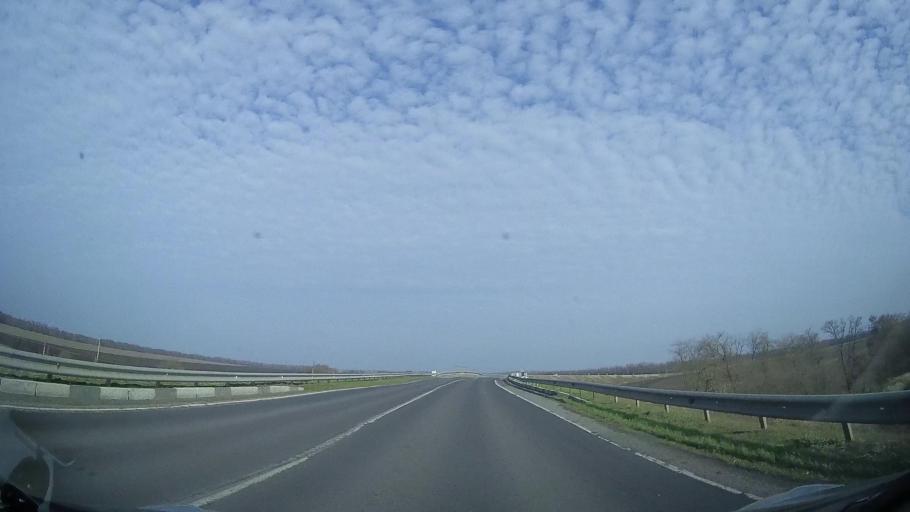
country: RU
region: Rostov
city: Tselina
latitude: 46.5279
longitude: 41.1679
